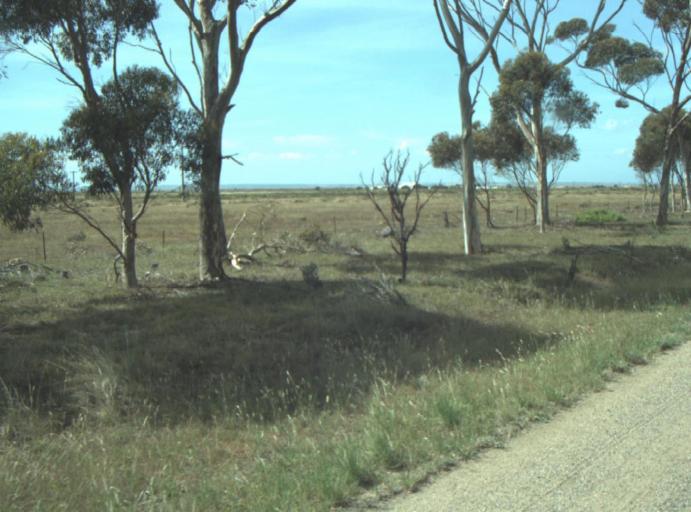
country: AU
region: Victoria
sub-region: Greater Geelong
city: Lara
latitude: -38.0600
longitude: 144.4268
